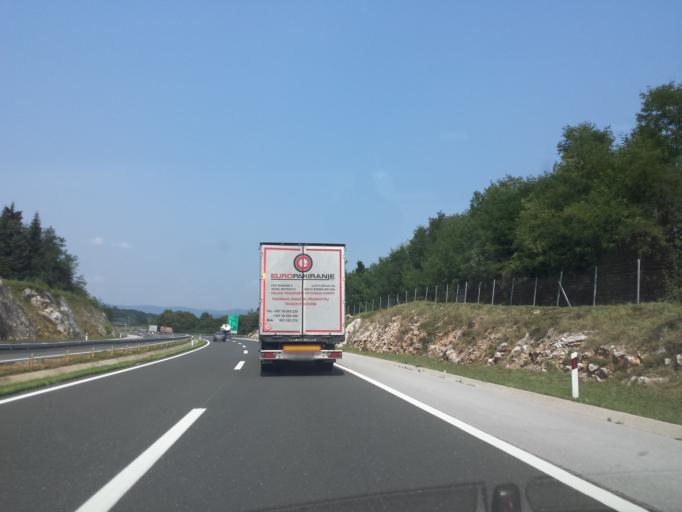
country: HR
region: Karlovacka
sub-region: Grad Ogulin
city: Ogulin
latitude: 45.3974
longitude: 15.2570
